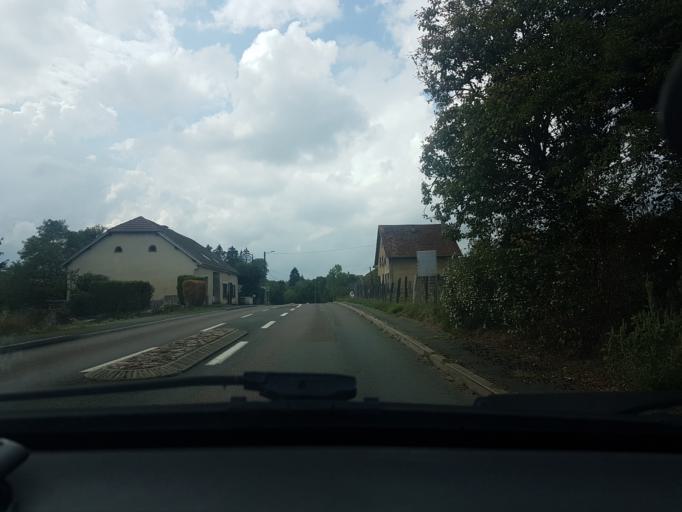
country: FR
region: Franche-Comte
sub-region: Departement du Doubs
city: Arcey
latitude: 47.5523
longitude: 6.5791
